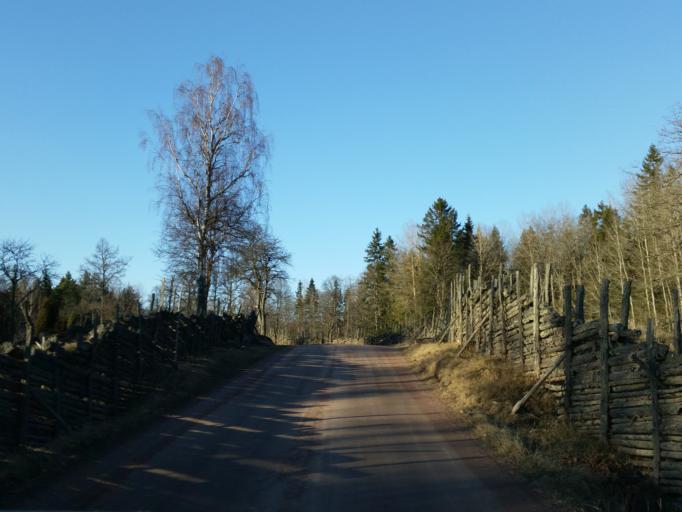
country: SE
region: Kalmar
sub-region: Oskarshamns Kommun
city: Oskarshamn
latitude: 57.3403
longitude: 16.4699
